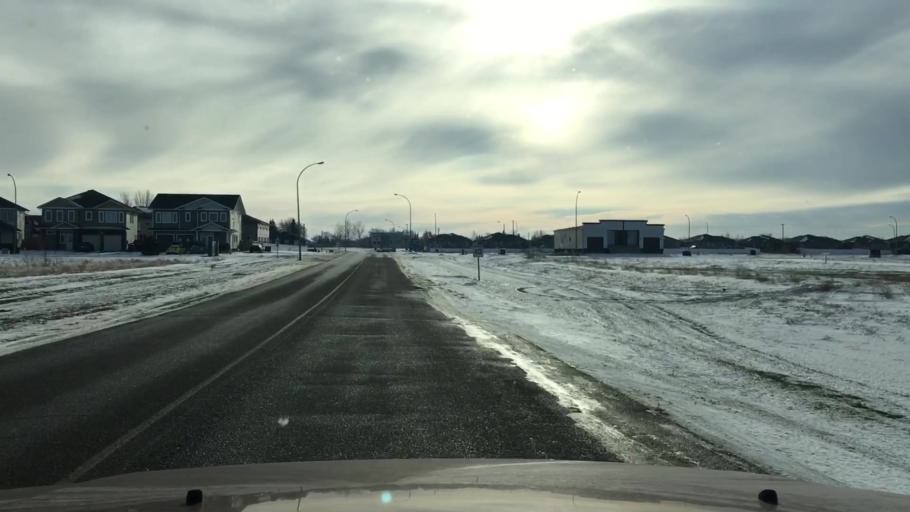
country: CA
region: Saskatchewan
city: Pilot Butte
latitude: 50.4871
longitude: -104.4202
